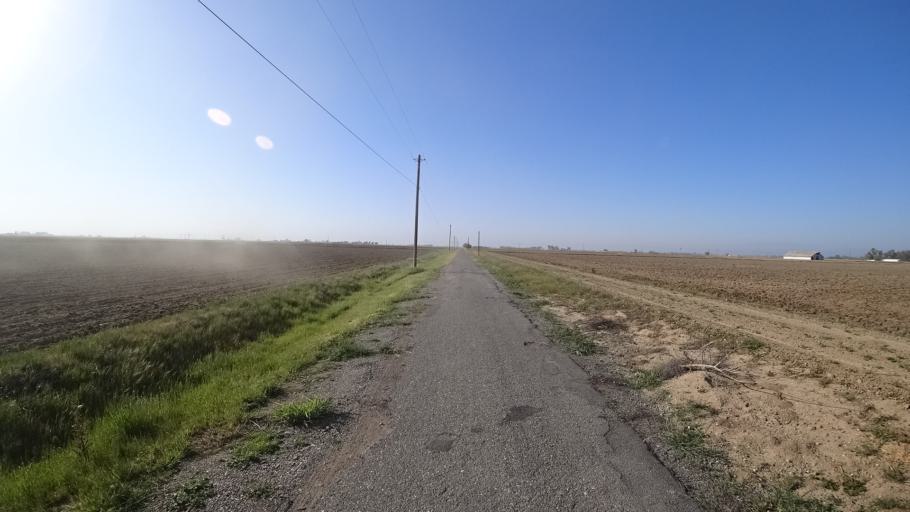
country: US
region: California
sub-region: Glenn County
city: Willows
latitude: 39.5582
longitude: -122.1321
